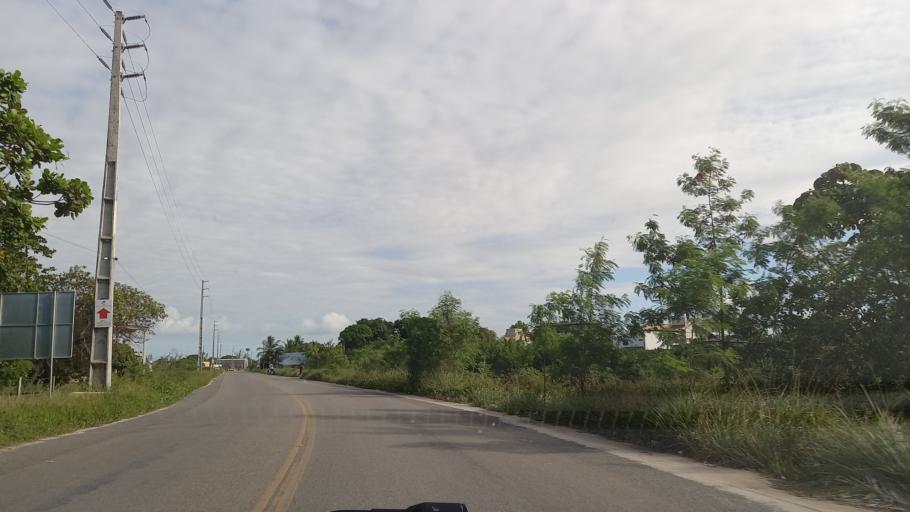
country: BR
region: Pernambuco
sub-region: Tamandare
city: Tamandare
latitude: -8.7220
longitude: -35.0955
